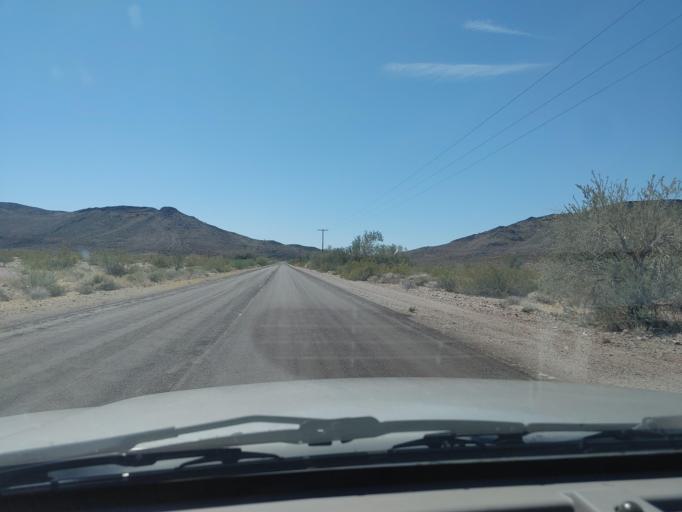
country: US
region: Arizona
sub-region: Maricopa County
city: Gila Bend
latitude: 33.0106
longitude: -113.3404
